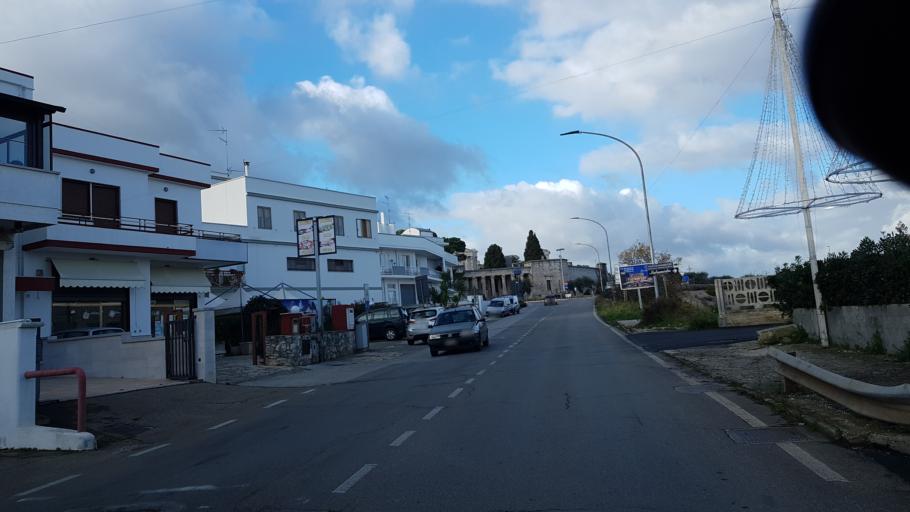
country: IT
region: Apulia
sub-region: Provincia di Bari
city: Alberobello
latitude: 40.7899
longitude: 17.2433
